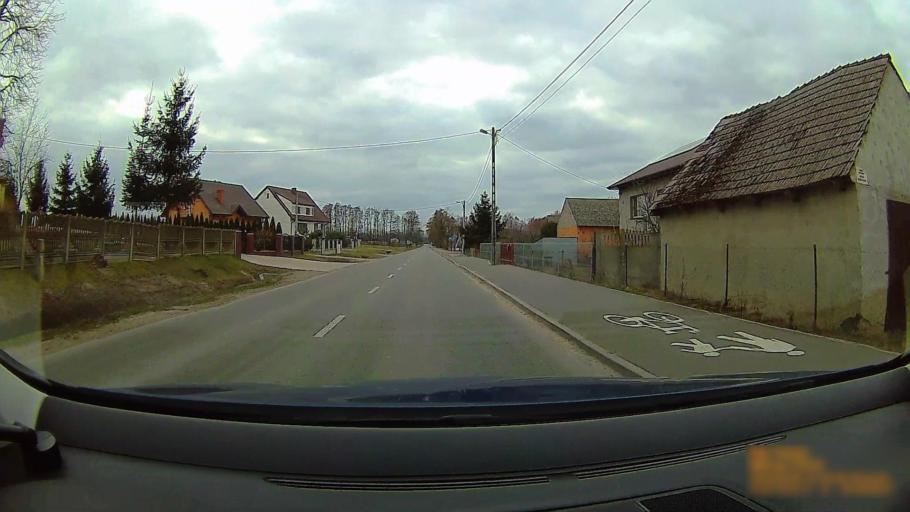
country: PL
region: Greater Poland Voivodeship
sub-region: Powiat koninski
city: Rzgow Pierwszy
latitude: 52.1757
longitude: 18.0942
